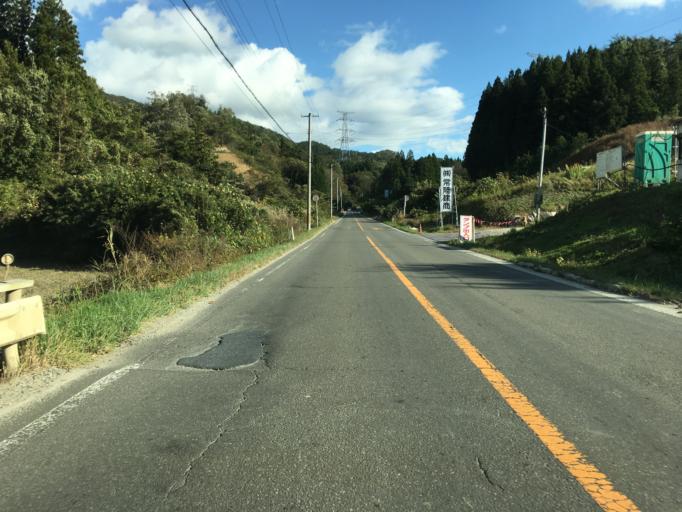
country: JP
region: Miyagi
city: Marumori
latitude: 37.8602
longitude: 140.8438
